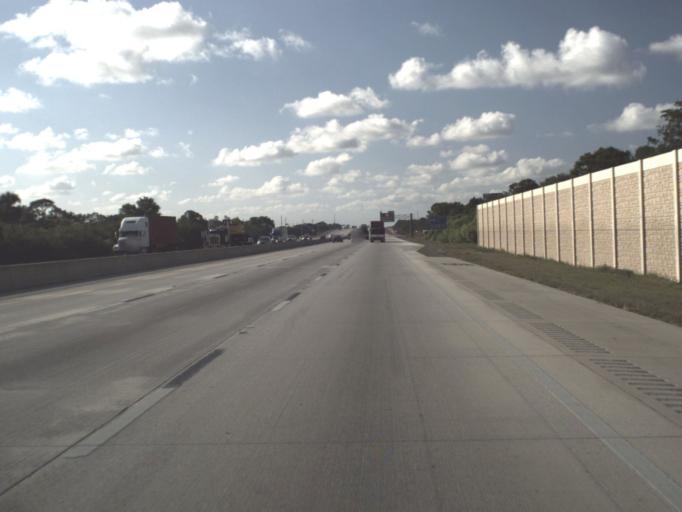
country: US
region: Florida
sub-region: Brevard County
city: Cocoa West
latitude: 28.3533
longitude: -80.7902
